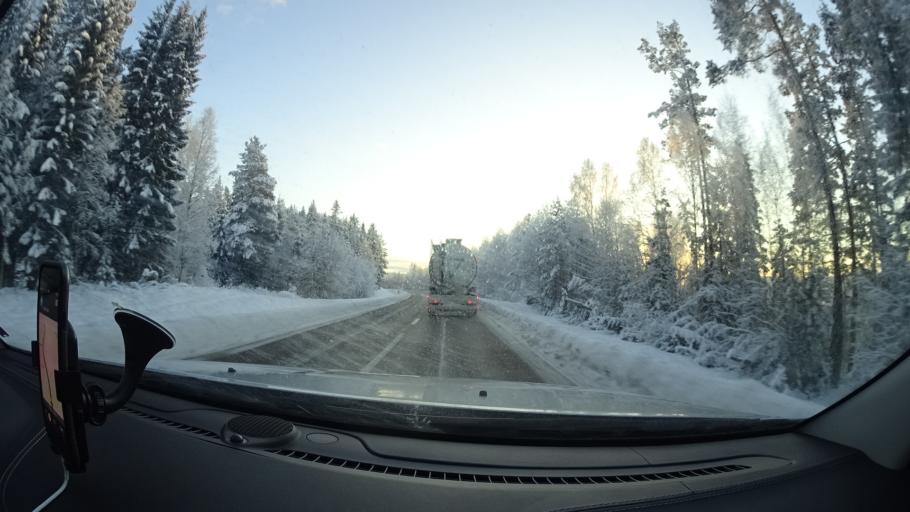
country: SE
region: Jaemtland
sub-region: Ragunda Kommun
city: Hammarstrand
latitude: 62.9483
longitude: 16.6926
